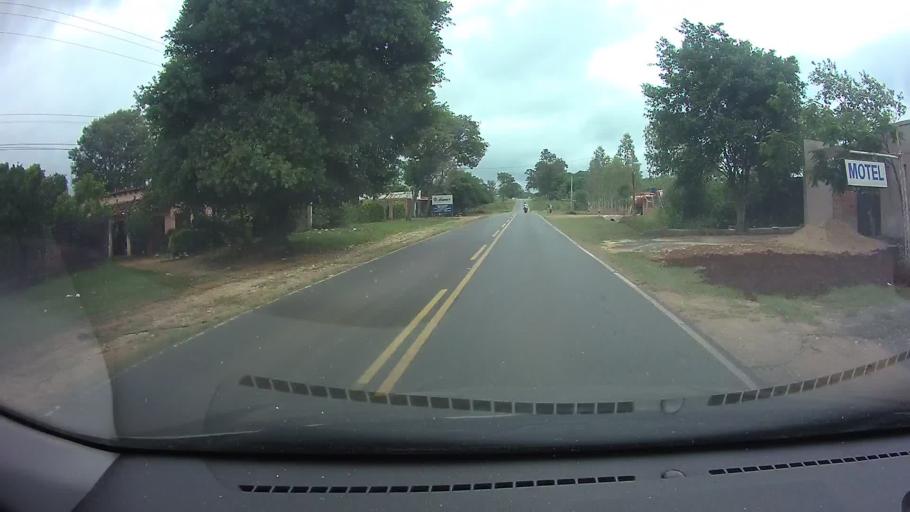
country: PY
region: Central
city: Guarambare
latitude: -25.5030
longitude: -57.4823
